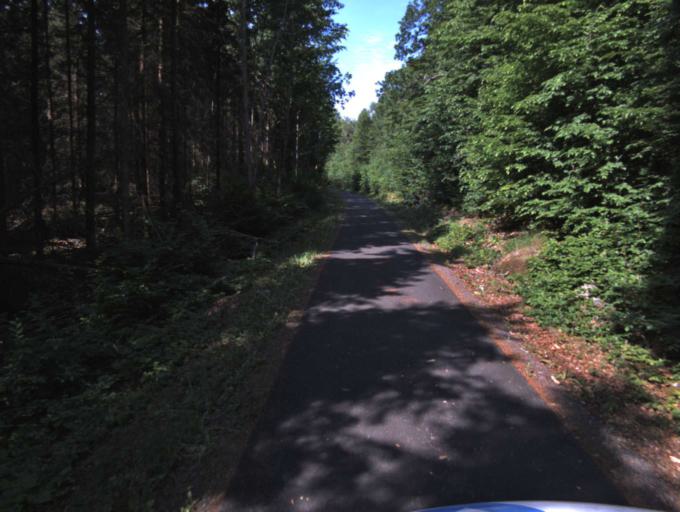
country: SE
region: Skane
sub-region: Kristianstads Kommun
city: Tollarp
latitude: 56.1787
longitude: 14.2845
